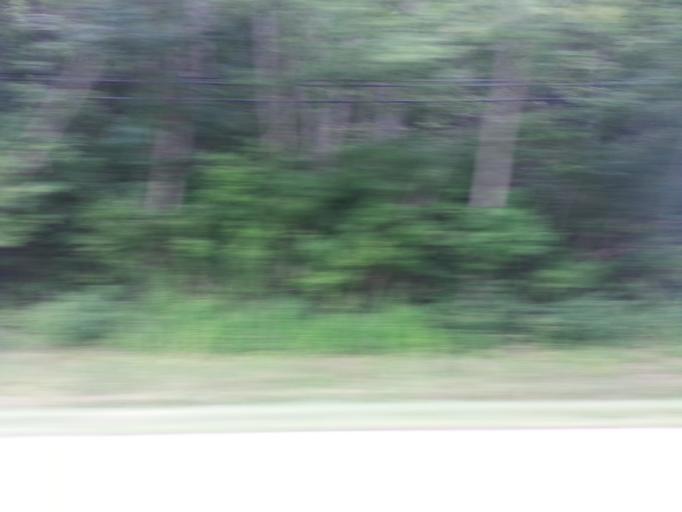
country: US
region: Ohio
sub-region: Brown County
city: Ripley
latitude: 38.7089
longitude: -83.8151
